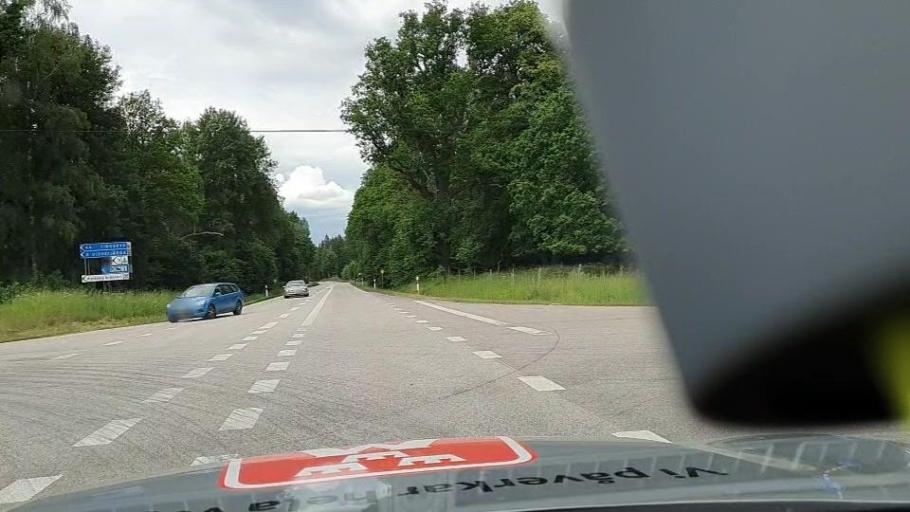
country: SE
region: Kalmar
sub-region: Emmaboda Kommun
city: Emmaboda
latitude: 56.5343
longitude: 15.6125
